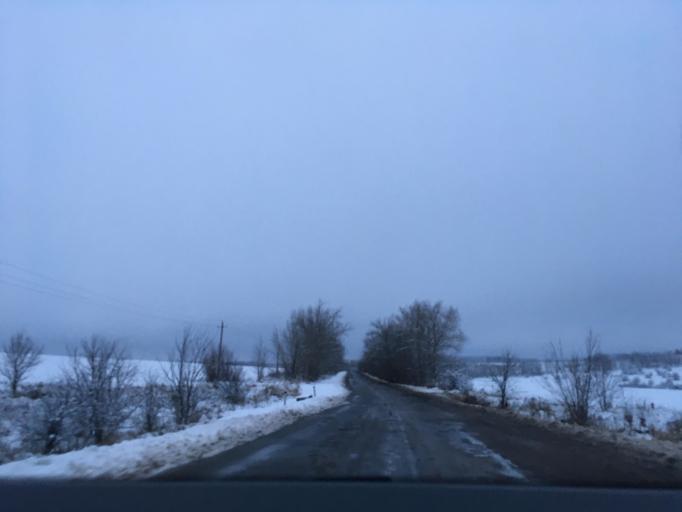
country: RU
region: Voronezj
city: Verkhniy Mamon
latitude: 50.0537
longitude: 40.2504
